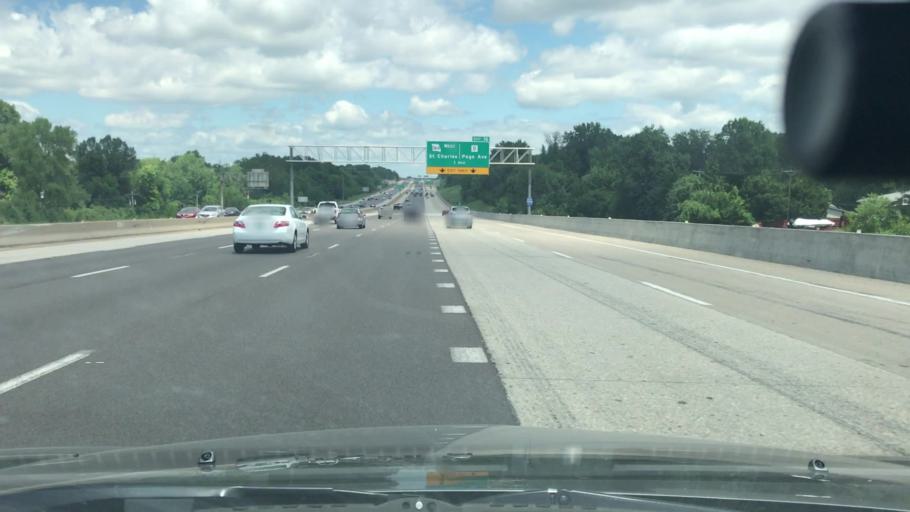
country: US
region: Missouri
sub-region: Saint Louis County
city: Creve Coeur
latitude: 38.6785
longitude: -90.4494
